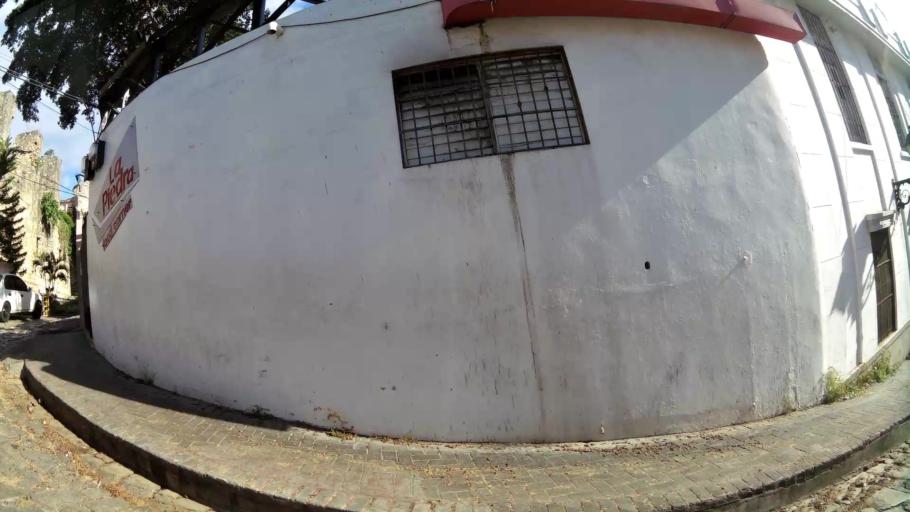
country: DO
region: Nacional
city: San Carlos
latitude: 18.4767
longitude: -69.8853
